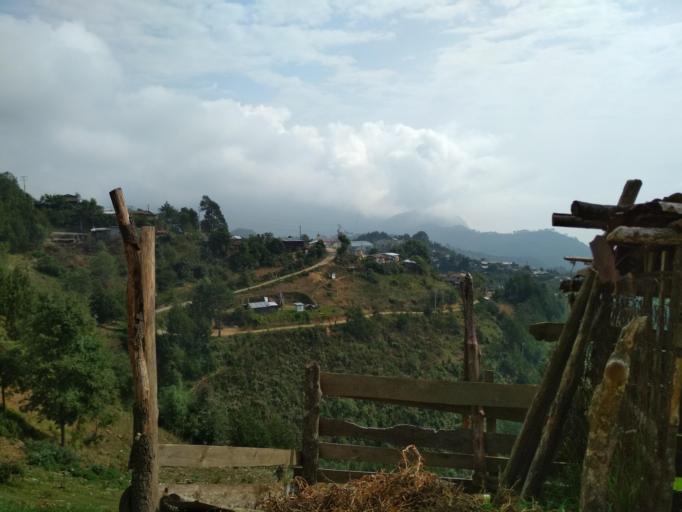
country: MX
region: Veracruz
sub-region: Soledad Atzompa
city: Tlatilpa
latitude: 18.7505
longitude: -97.1536
